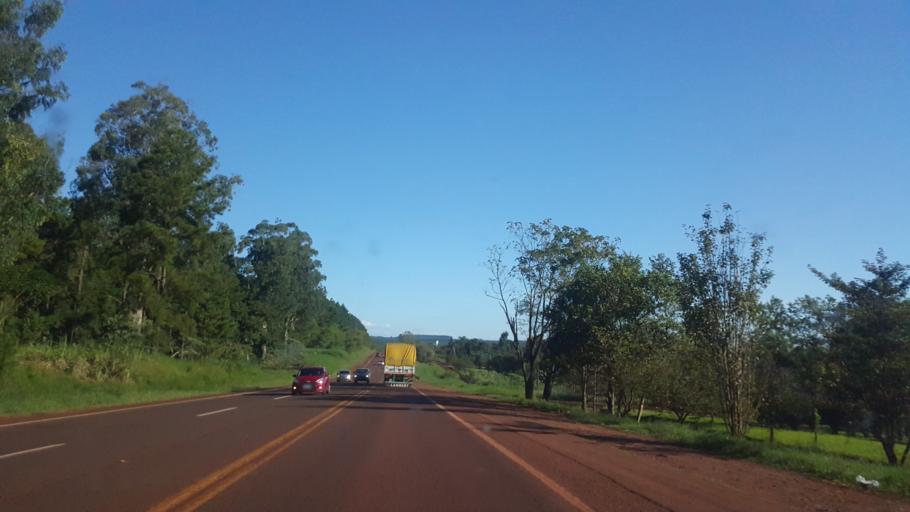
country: AR
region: Misiones
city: Puerto Esperanza
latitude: -26.1824
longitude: -54.5896
